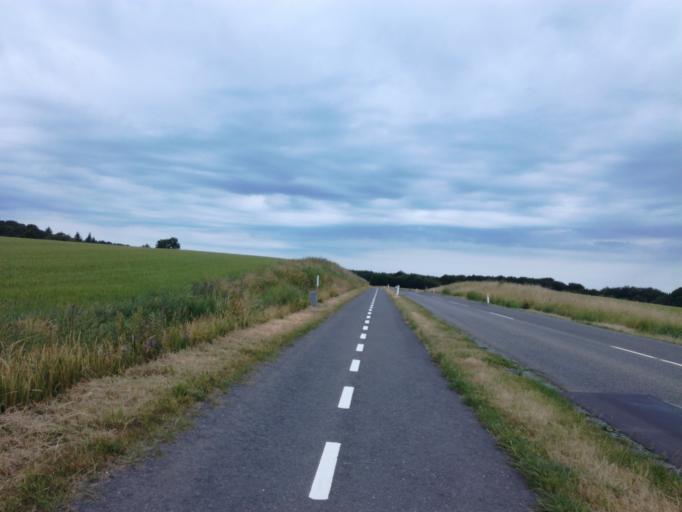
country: DK
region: South Denmark
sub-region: Vejle Kommune
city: Borkop
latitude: 55.6702
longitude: 9.6200
